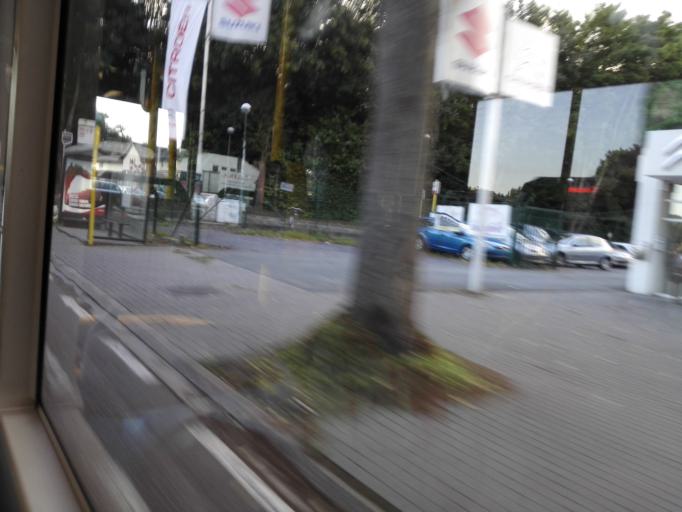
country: BE
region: Flanders
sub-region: Provincie Vlaams-Brabant
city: Wezembeek-Oppem
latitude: 50.8453
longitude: 4.5005
